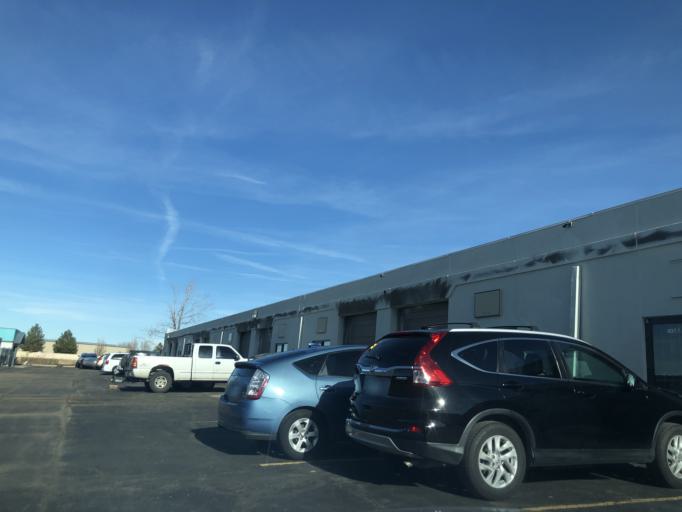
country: US
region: Colorado
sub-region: Adams County
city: Aurora
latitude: 39.7222
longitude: -104.8018
